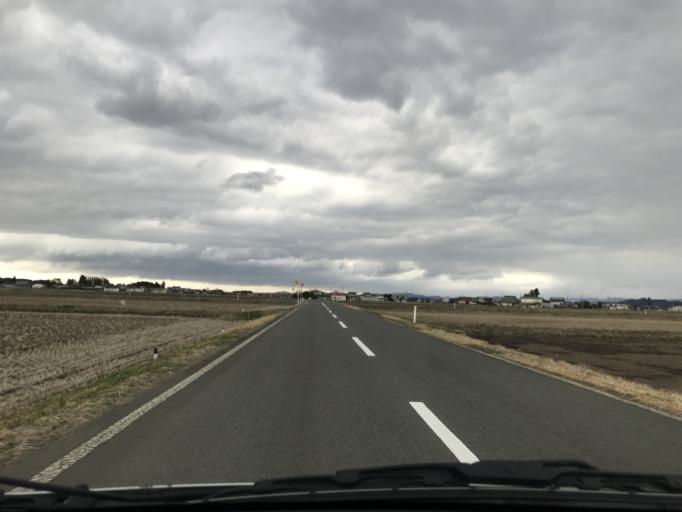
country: JP
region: Iwate
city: Mizusawa
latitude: 39.0974
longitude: 141.1627
